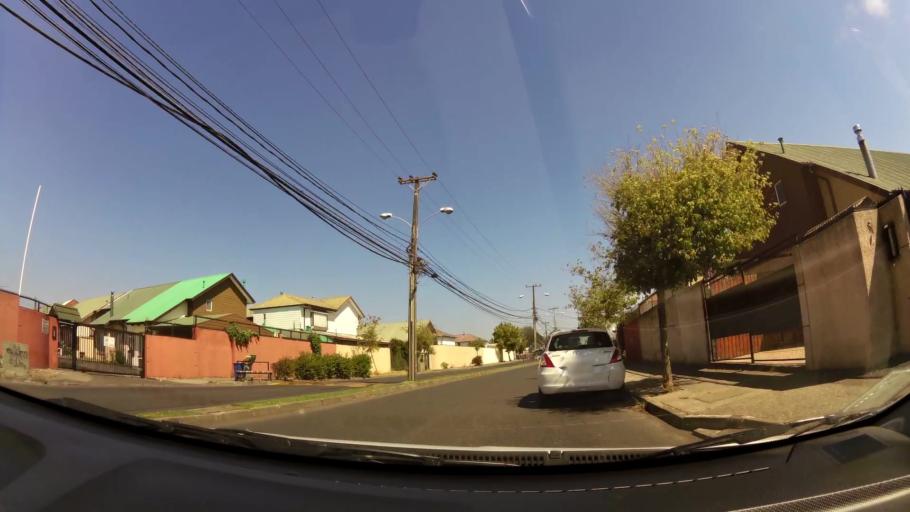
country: CL
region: Biobio
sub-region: Provincia de Concepcion
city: Concepcion
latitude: -36.7865
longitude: -73.0431
